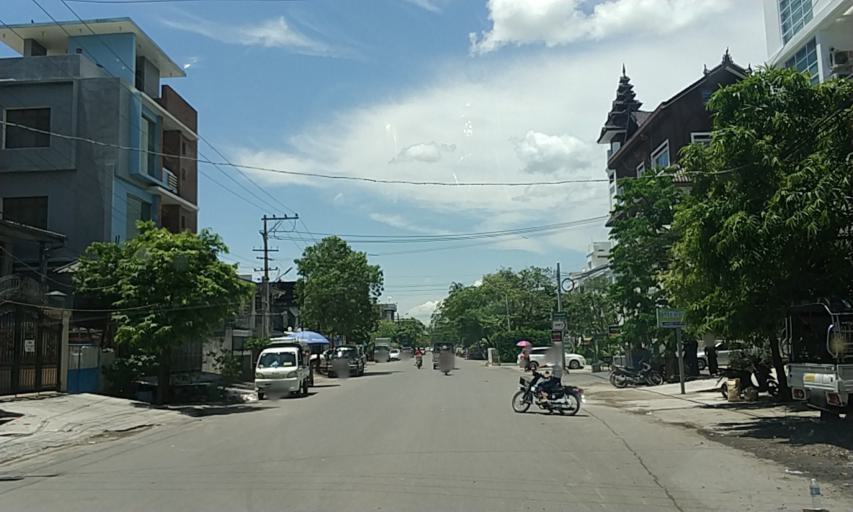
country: MM
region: Mandalay
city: Mandalay
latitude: 21.9781
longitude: 96.0969
